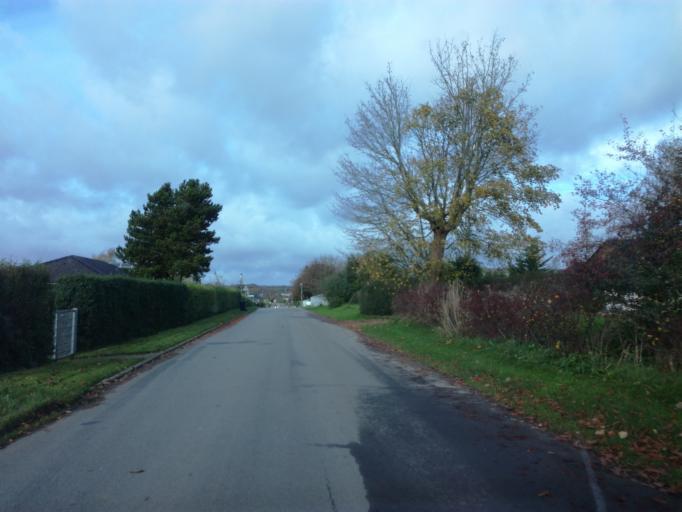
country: DK
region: South Denmark
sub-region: Vejle Kommune
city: Brejning
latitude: 55.6599
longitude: 9.6793
